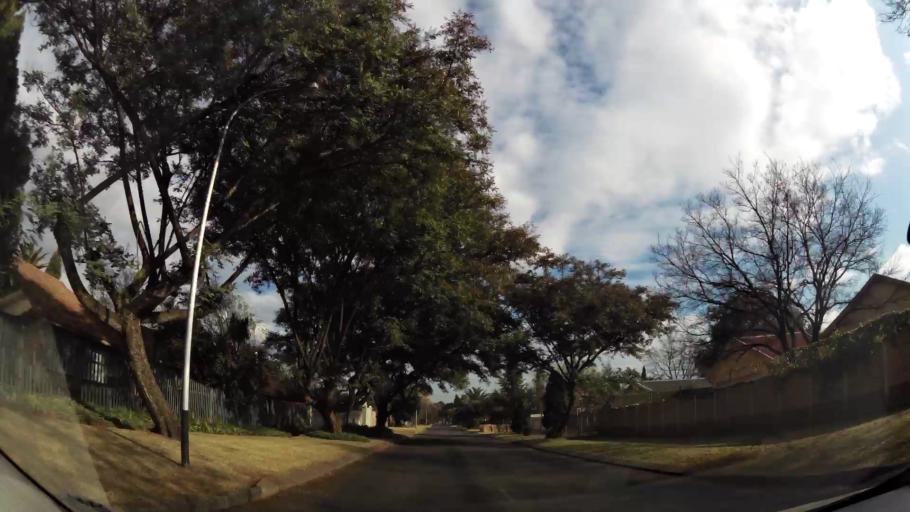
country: ZA
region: Gauteng
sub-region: Sedibeng District Municipality
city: Meyerton
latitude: -26.5518
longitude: 28.0316
